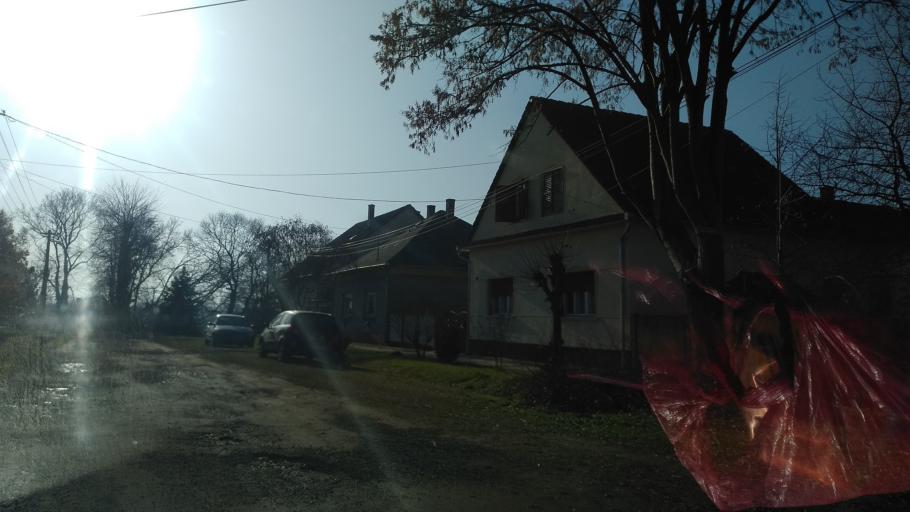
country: HU
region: Somogy
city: Barcs
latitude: 45.9597
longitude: 17.4821
